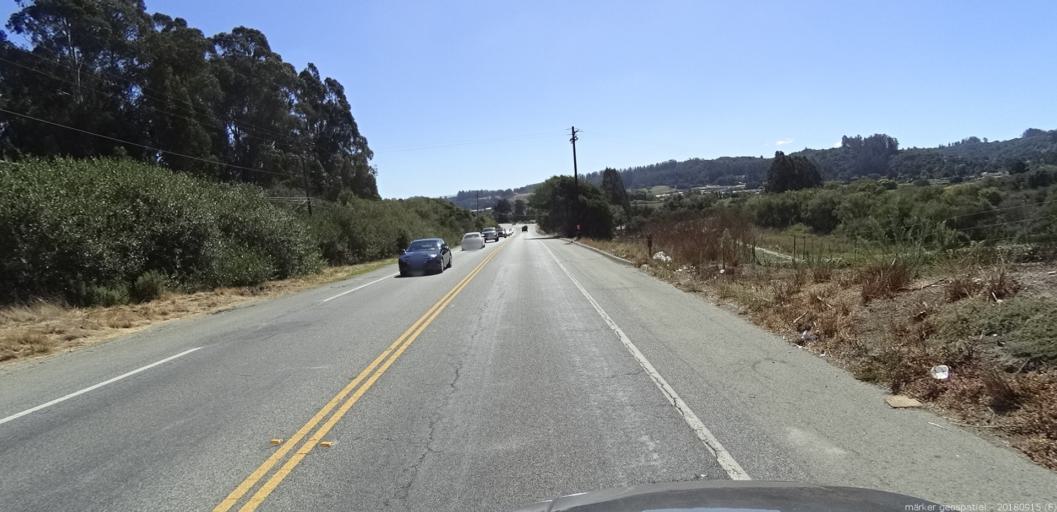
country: US
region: California
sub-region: Monterey County
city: Las Lomas
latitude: 36.8631
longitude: -121.7102
